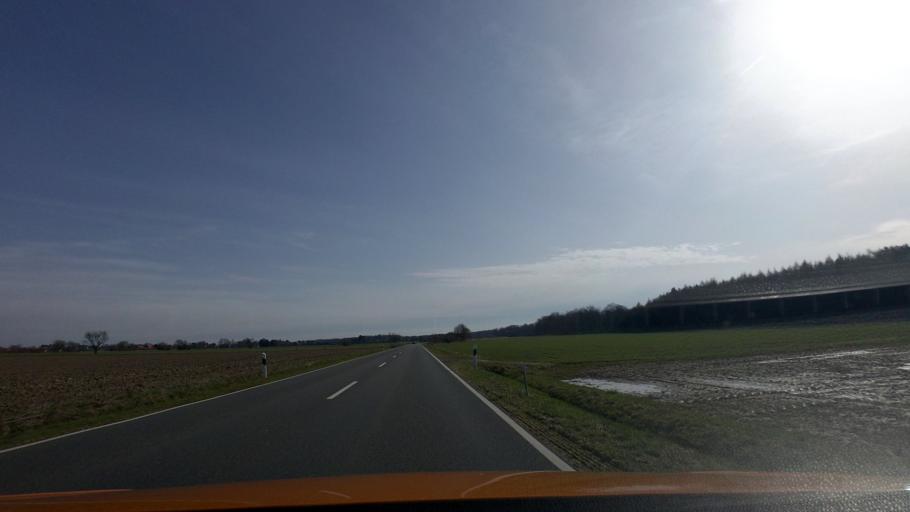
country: DE
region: Lower Saxony
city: Wiedensahl
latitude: 52.3730
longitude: 9.1044
